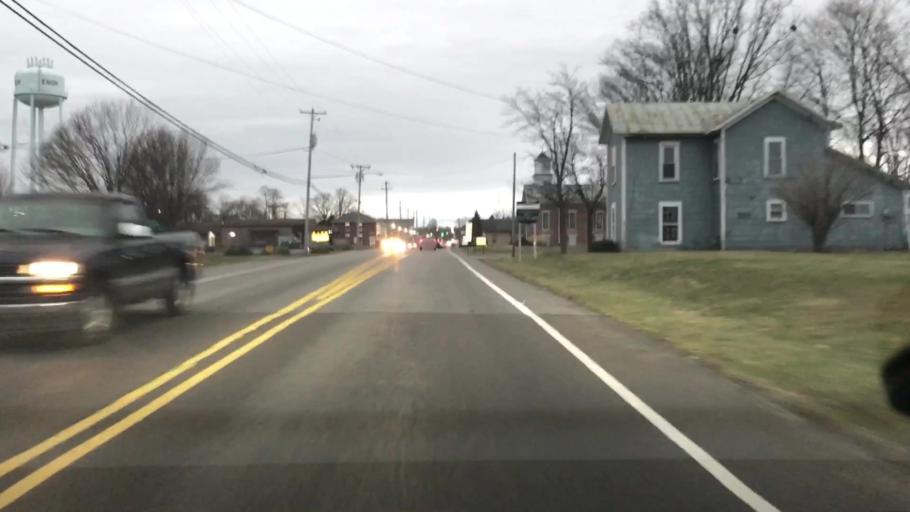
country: US
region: Ohio
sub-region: Clark County
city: Enon
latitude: 39.8765
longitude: -83.9405
